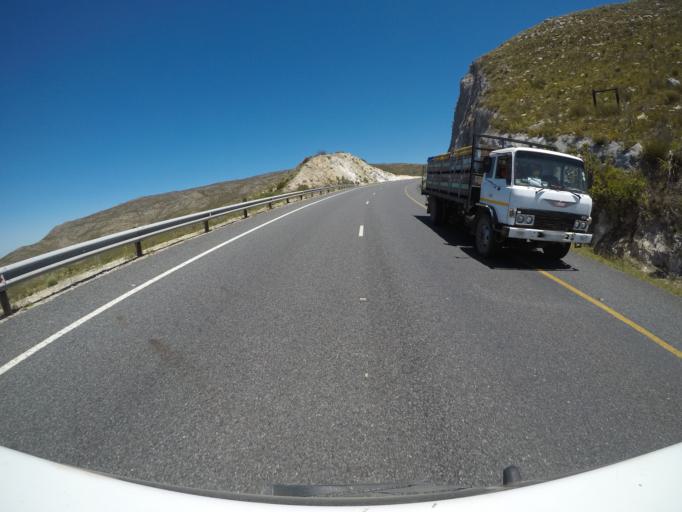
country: ZA
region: Western Cape
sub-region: Overberg District Municipality
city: Grabouw
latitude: -34.2218
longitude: 19.1815
